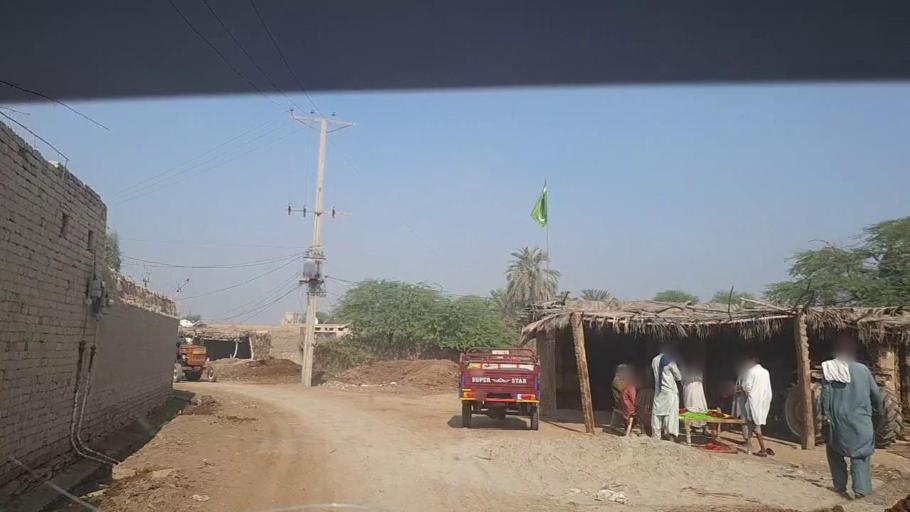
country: PK
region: Sindh
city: Khairpur
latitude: 27.4710
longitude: 68.7132
